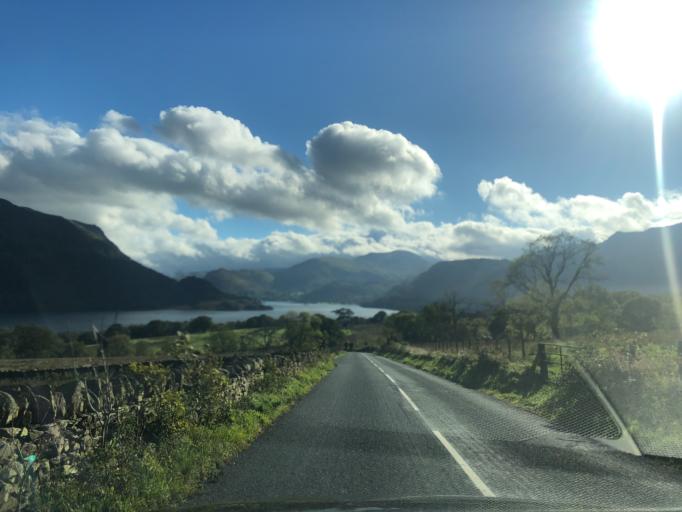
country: GB
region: England
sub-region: Cumbria
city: Ambleside
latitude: 54.5752
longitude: -2.9348
